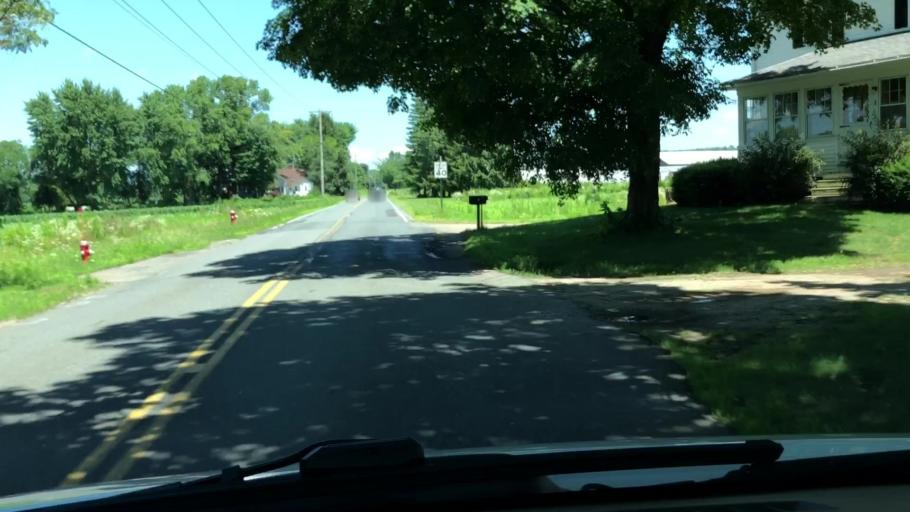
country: US
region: Massachusetts
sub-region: Hampshire County
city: North Amherst
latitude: 42.4001
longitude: -72.5460
